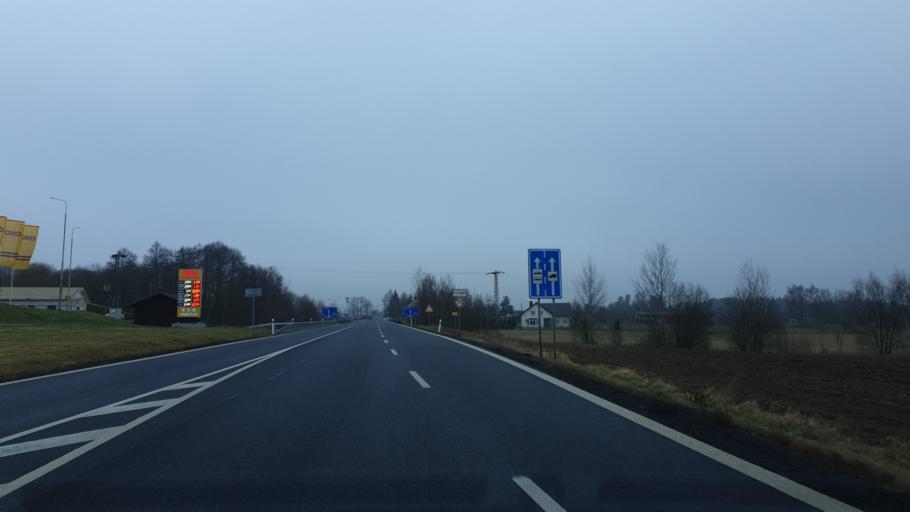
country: CZ
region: Karlovarsky
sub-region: Okres Cheb
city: Skalna
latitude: 50.1627
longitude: 12.3194
